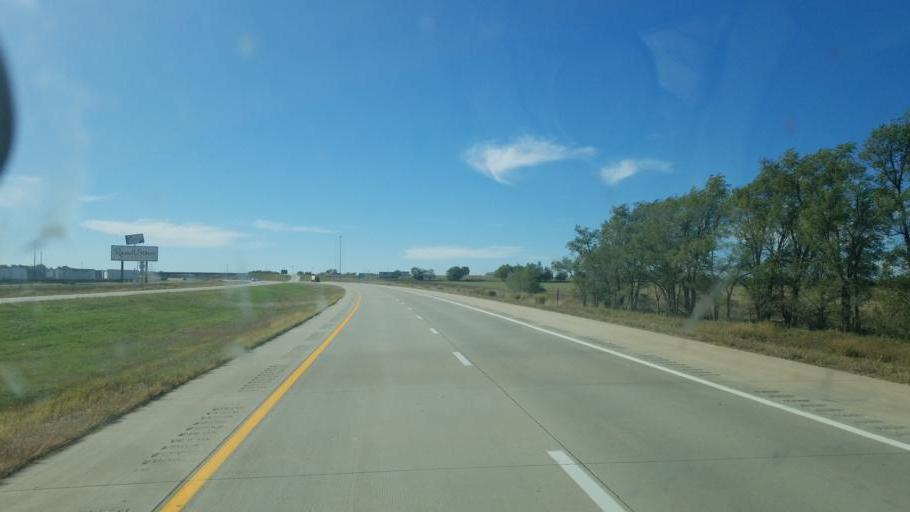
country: US
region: Kansas
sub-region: Dickinson County
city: Abilene
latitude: 38.9365
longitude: -97.2512
